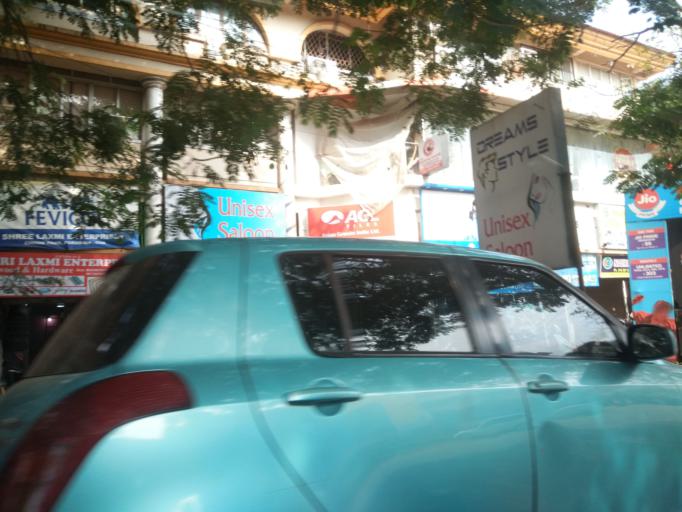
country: IN
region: Goa
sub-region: North Goa
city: Serula
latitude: 15.5350
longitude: 73.8209
